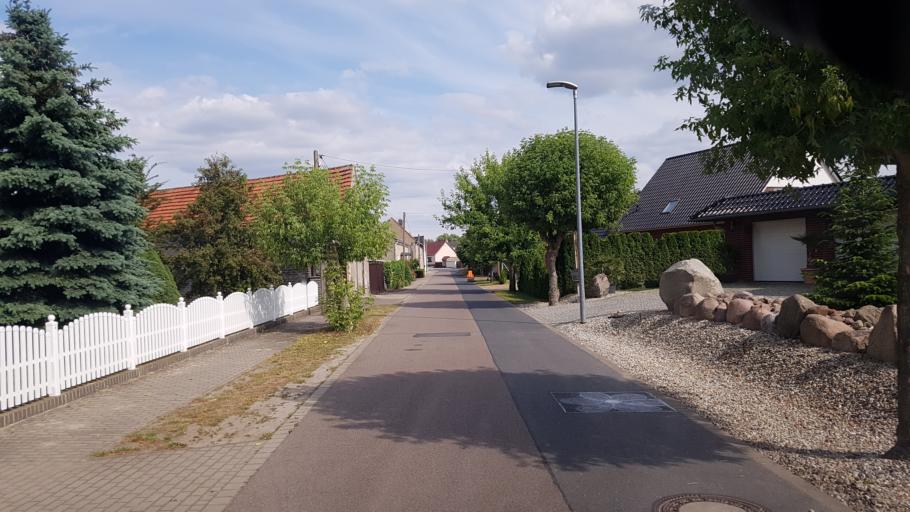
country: DE
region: Brandenburg
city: Herzberg
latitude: 51.7616
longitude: 13.2511
